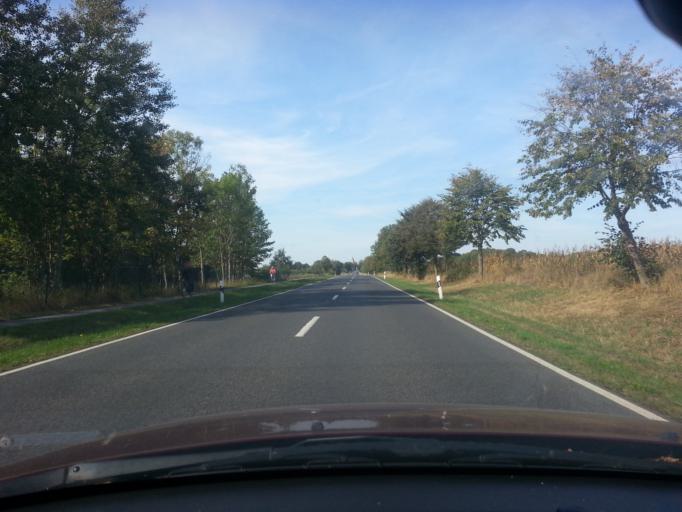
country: DE
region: Saxony
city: Goerlitz
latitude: 51.1192
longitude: 14.9528
